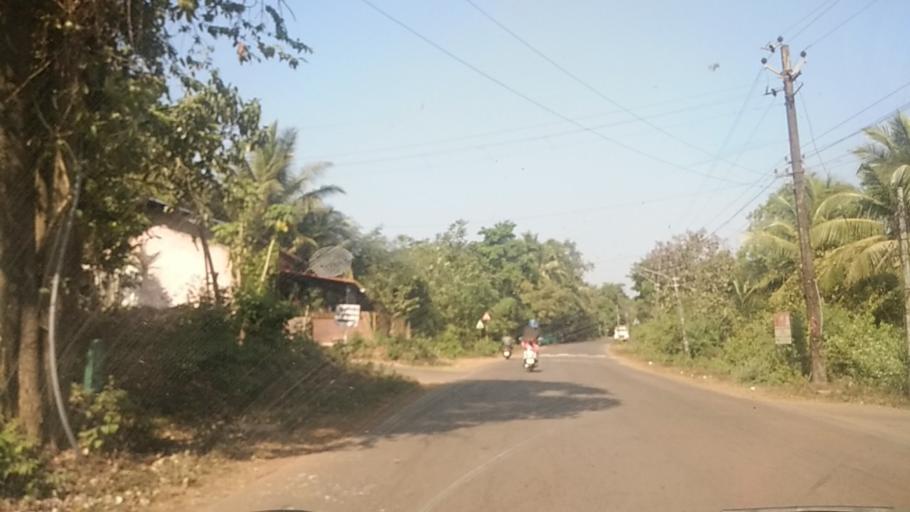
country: IN
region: Goa
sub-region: South Goa
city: Sanvordem
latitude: 15.2367
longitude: 74.1249
